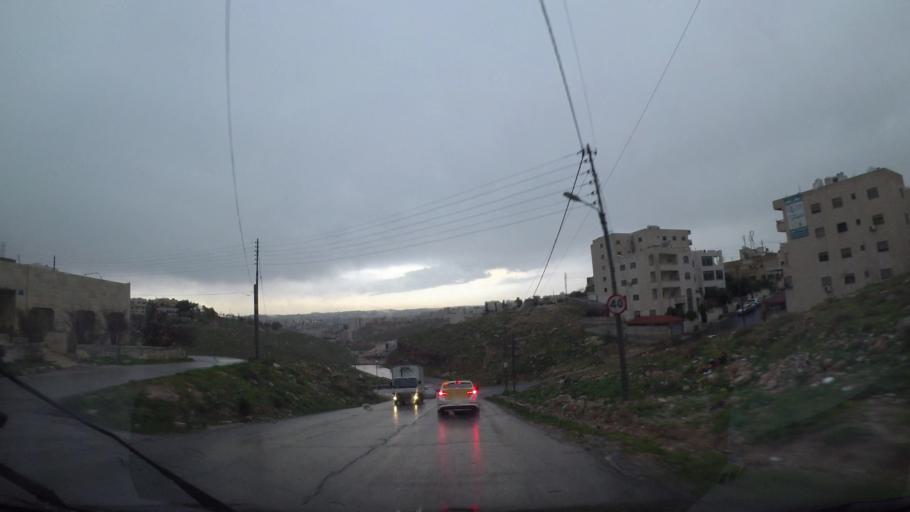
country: JO
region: Amman
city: Amman
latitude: 31.9989
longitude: 35.9688
